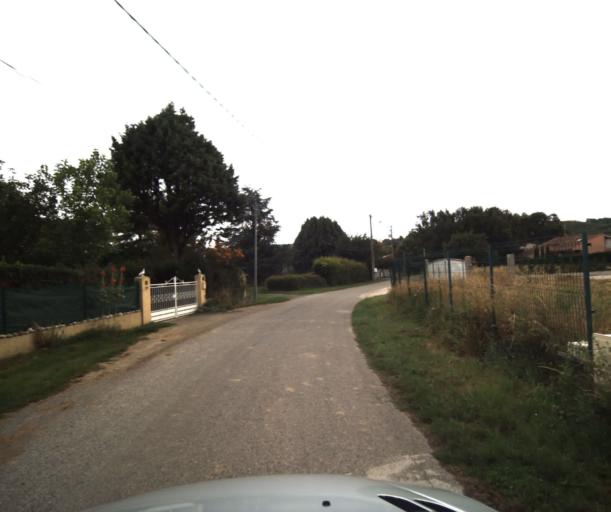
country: FR
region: Midi-Pyrenees
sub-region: Departement de la Haute-Garonne
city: Labarthe-sur-Leze
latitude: 43.4735
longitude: 1.4122
